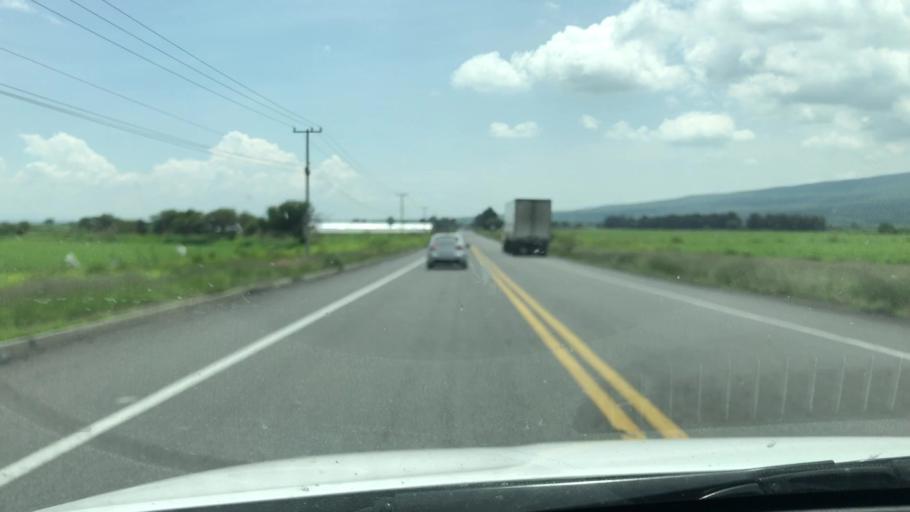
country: MX
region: Michoacan
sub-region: Yurecuaro
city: Yurecuaro
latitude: 20.3381
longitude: -102.1877
